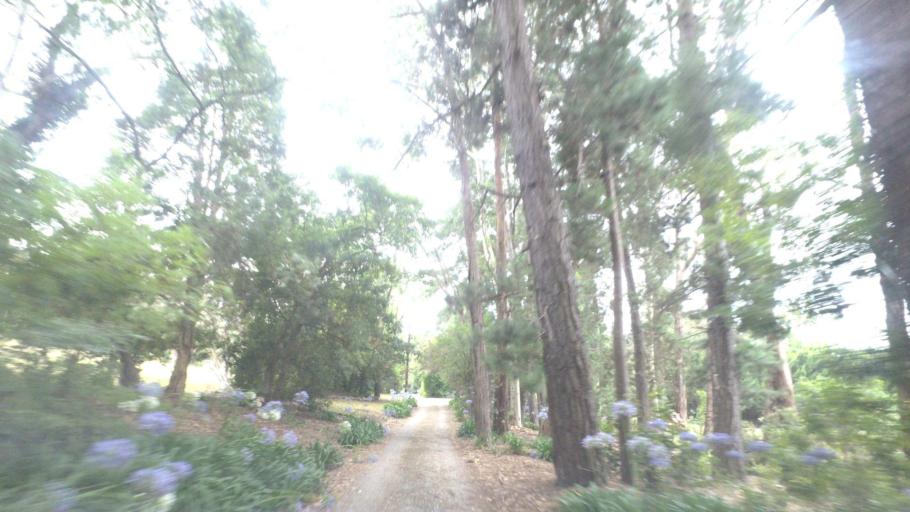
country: AU
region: Victoria
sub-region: Yarra Ranges
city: Mount Evelyn
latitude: -37.7647
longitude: 145.3839
